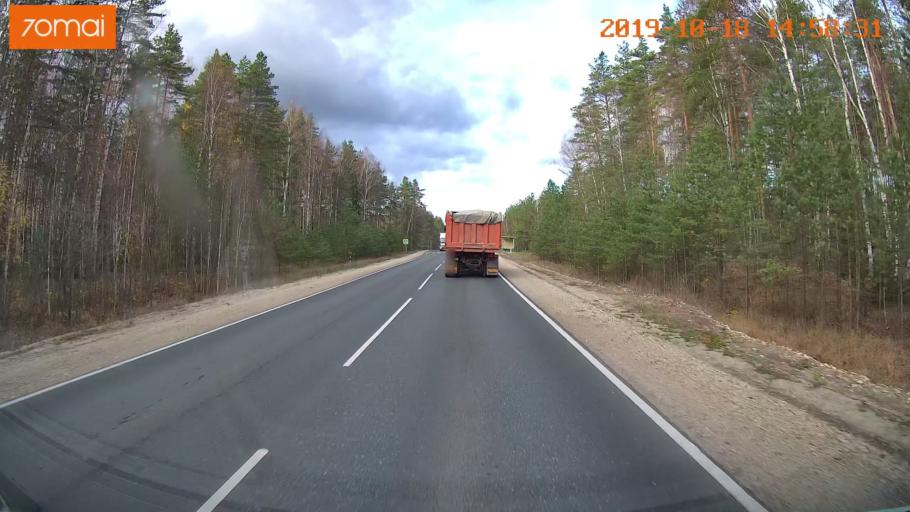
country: RU
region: Vladimir
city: Kurlovo
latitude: 55.4912
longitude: 40.5768
